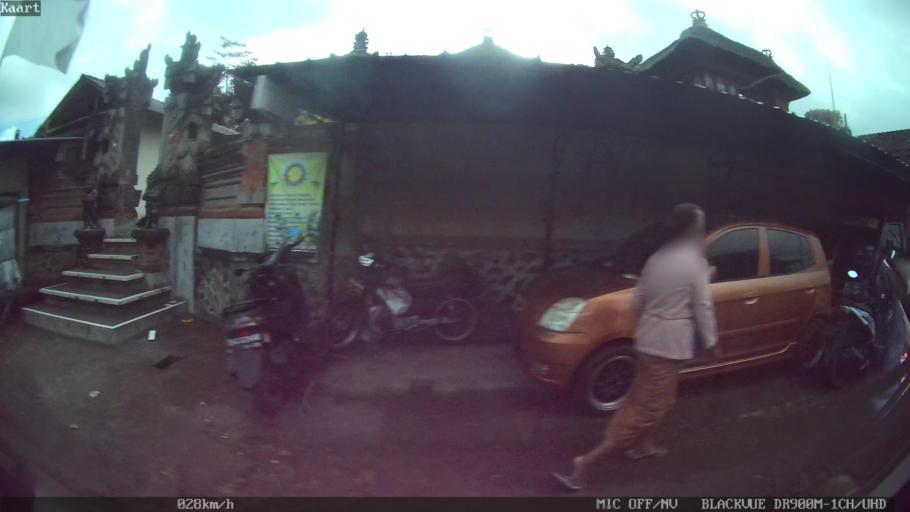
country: ID
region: Bali
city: Banjar Pesalakan
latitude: -8.4847
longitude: 115.3049
